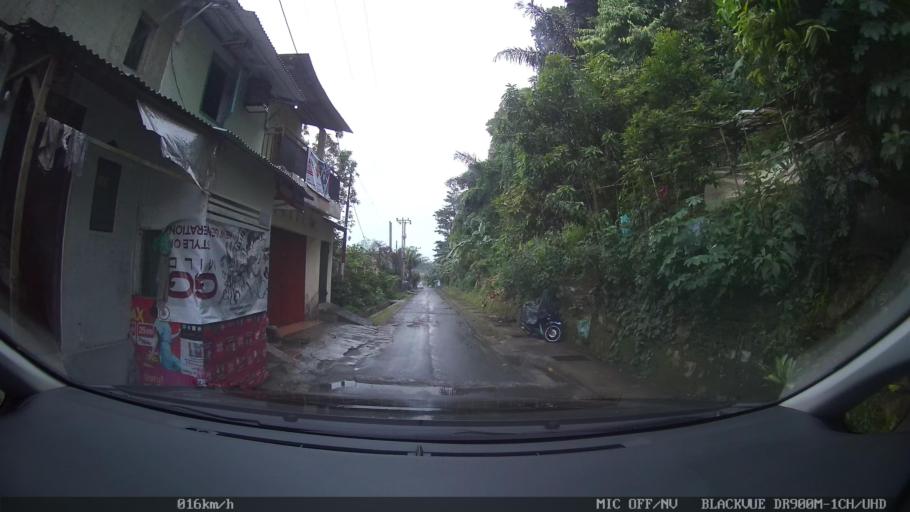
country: ID
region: Lampung
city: Bandarlampung
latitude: -5.4369
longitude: 105.2808
